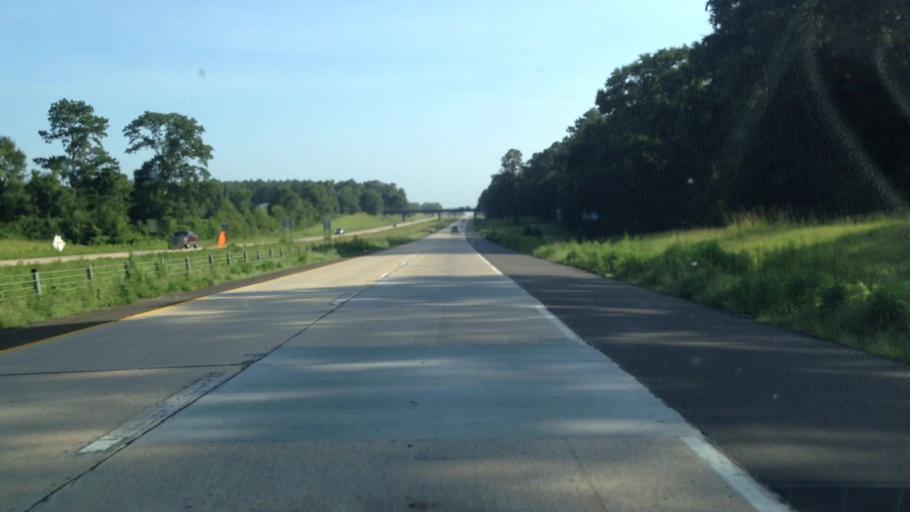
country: US
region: Mississippi
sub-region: Pike County
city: Summit
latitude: 31.2790
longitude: -90.4788
